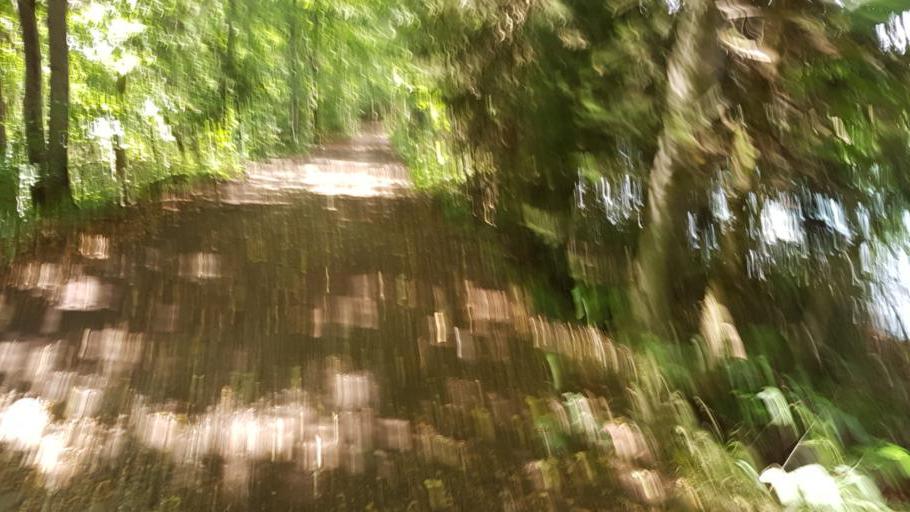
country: CH
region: Bern
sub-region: Bern-Mittelland District
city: Belp
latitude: 46.9127
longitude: 7.5061
